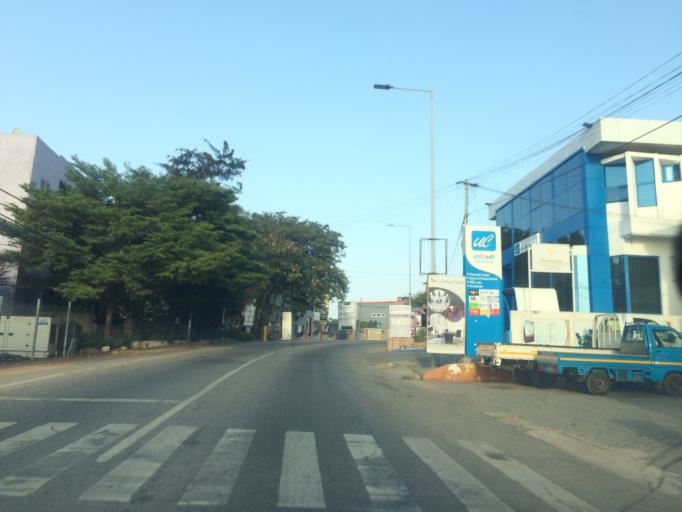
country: GH
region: Greater Accra
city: Accra
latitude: 5.5661
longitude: -0.2107
